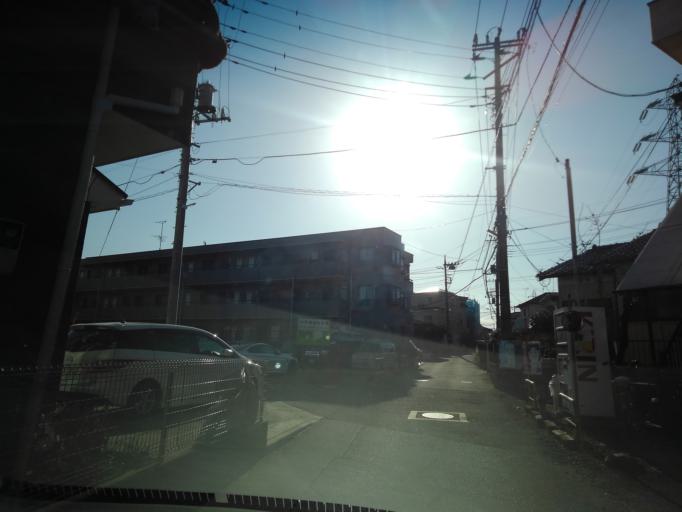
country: JP
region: Saitama
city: Tokorozawa
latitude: 35.7915
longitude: 139.4400
